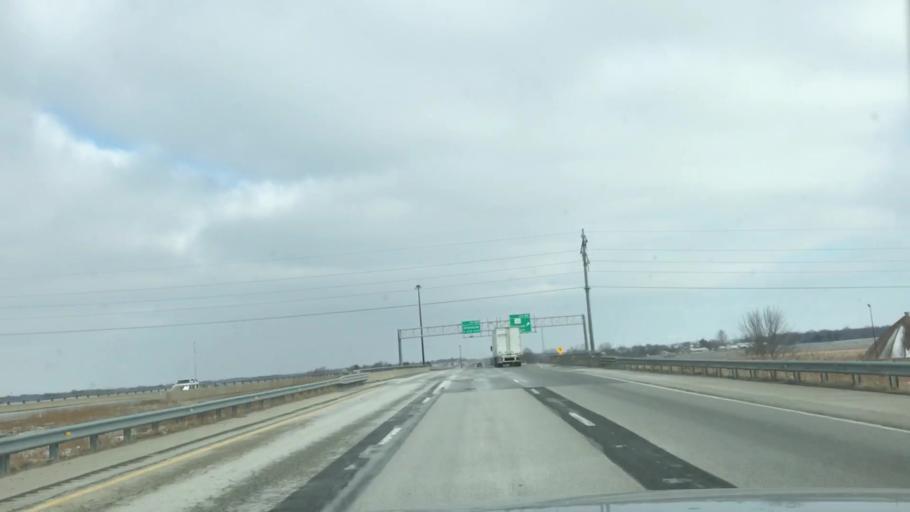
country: US
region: Illinois
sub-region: Sangamon County
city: Divernon
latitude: 39.5891
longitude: -89.6463
